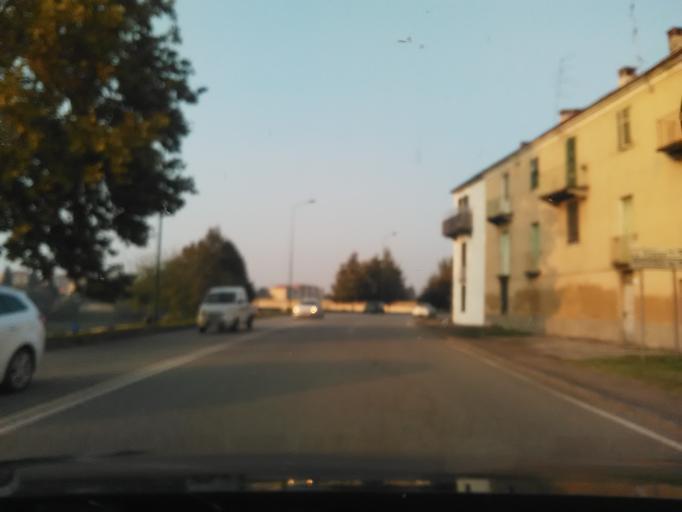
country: IT
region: Piedmont
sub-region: Provincia di Alessandria
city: Casale Monferrato
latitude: 45.1395
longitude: 8.4466
